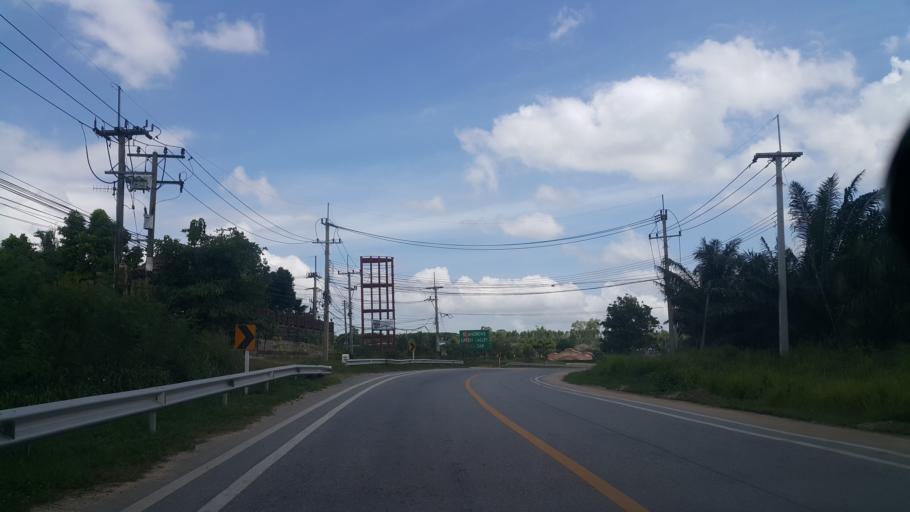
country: TH
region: Rayong
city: Ban Chang
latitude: 12.8119
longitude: 101.0594
